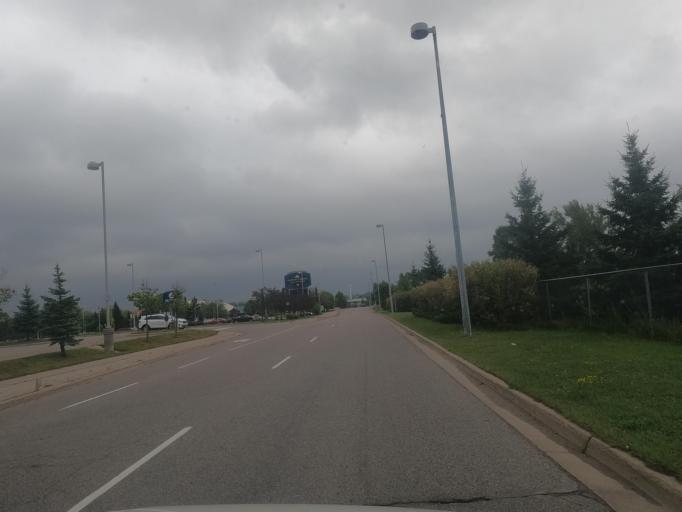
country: CA
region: Ontario
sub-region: Algoma
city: Sault Ste. Marie
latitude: 46.5170
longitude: -84.3471
